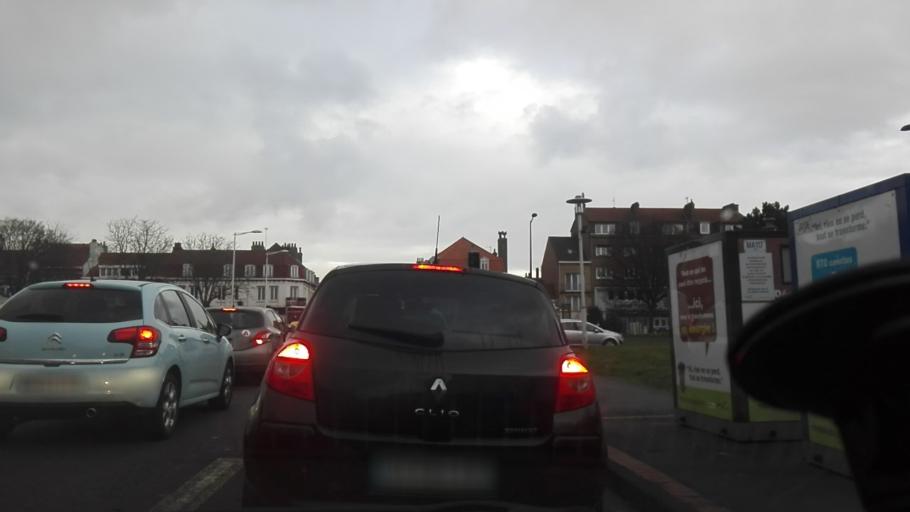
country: FR
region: Nord-Pas-de-Calais
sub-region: Departement du Nord
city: Coudekerque-Branche
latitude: 51.0435
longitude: 2.3973
